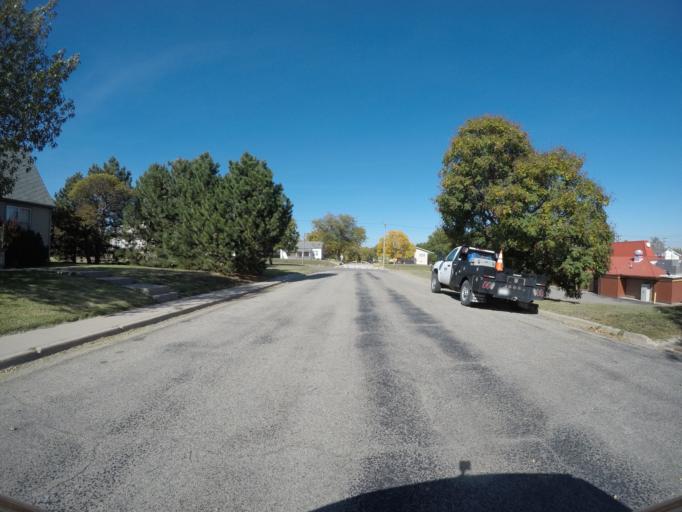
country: US
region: Kansas
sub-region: Phillips County
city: Phillipsburg
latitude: 39.7553
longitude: -99.3162
